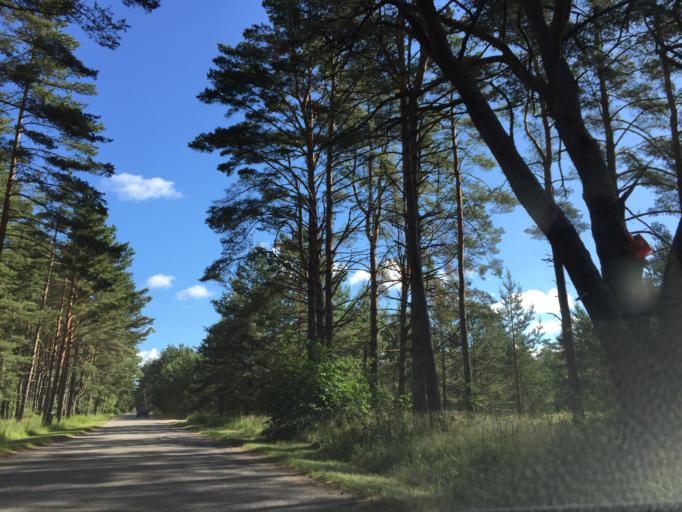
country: LV
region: Ventspils
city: Ventspils
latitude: 57.4438
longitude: 21.6205
